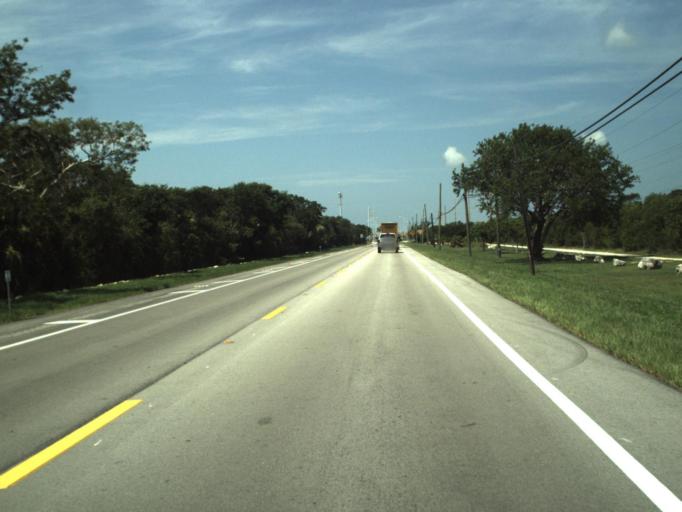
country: US
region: Florida
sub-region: Monroe County
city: Marathon
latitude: 24.7380
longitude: -81.0051
